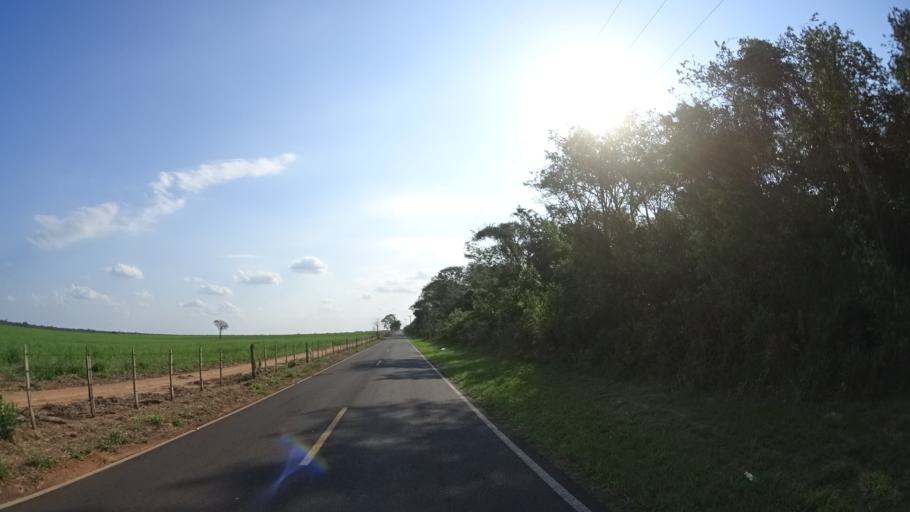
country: BR
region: Sao Paulo
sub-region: Urupes
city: Urupes
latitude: -21.3851
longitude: -49.4948
